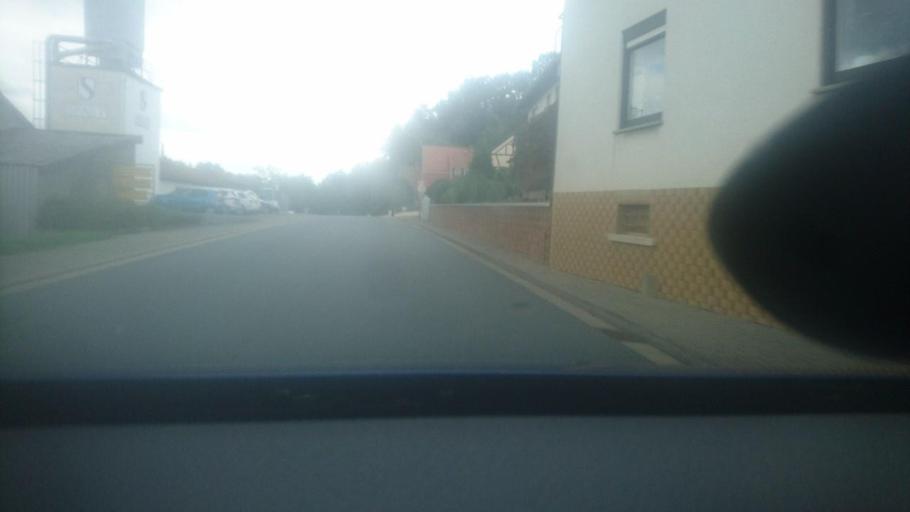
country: DE
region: Hesse
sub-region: Regierungsbezirk Darmstadt
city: Brensbach
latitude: 49.7477
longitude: 8.8872
